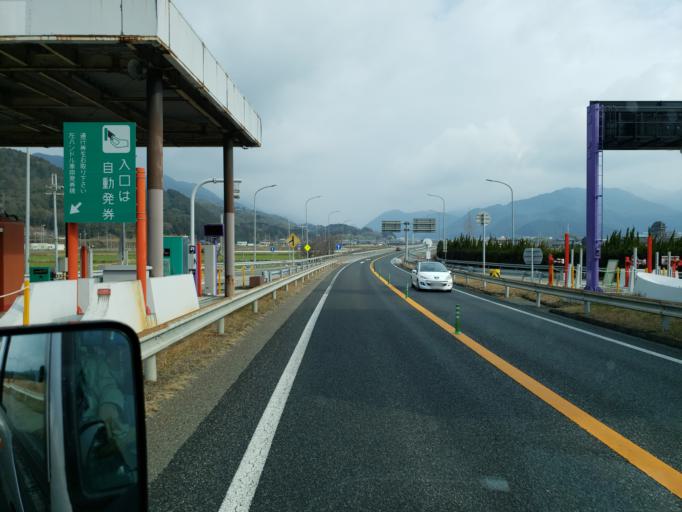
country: JP
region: Hyogo
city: Yamazakicho-nakabirose
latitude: 35.0589
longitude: 134.7640
